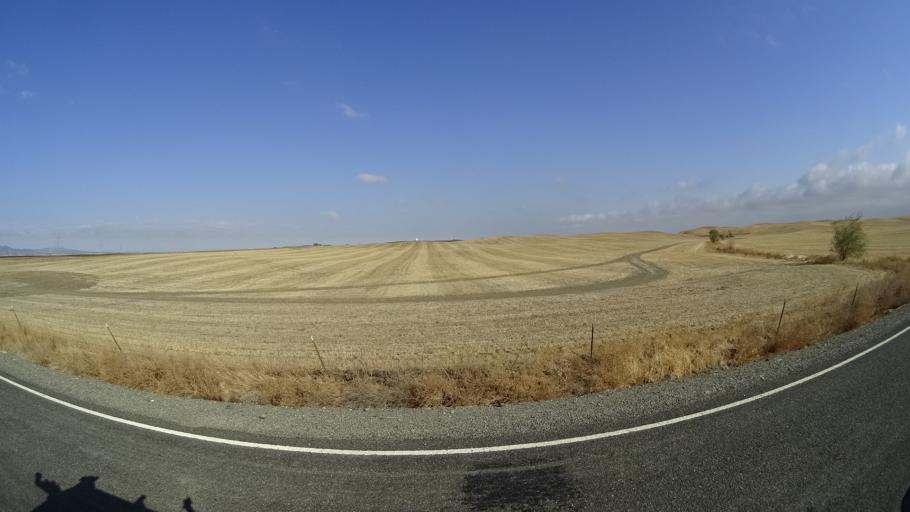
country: US
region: California
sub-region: Yolo County
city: Esparto
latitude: 38.7808
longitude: -121.9966
